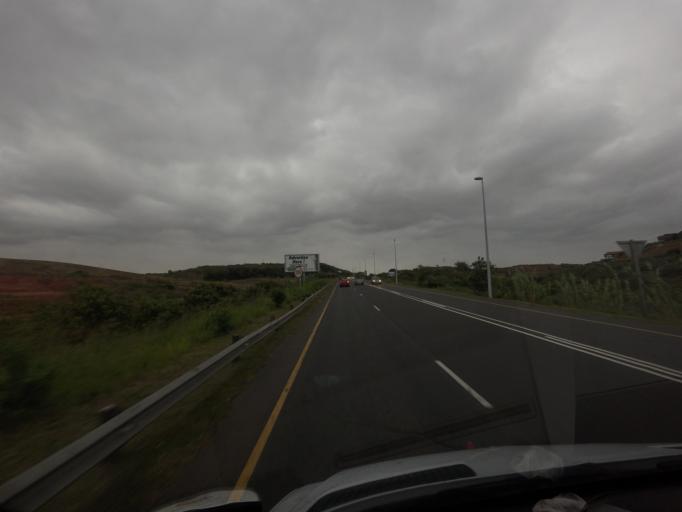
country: ZA
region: KwaZulu-Natal
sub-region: iLembe District Municipality
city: Ballitoville
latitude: -29.5627
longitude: 31.1833
